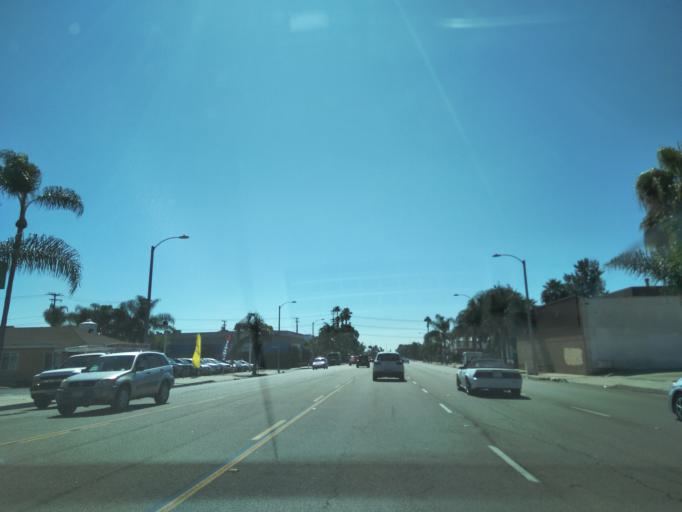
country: US
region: California
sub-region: Orange County
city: Santa Ana
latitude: 33.7146
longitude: -117.8680
